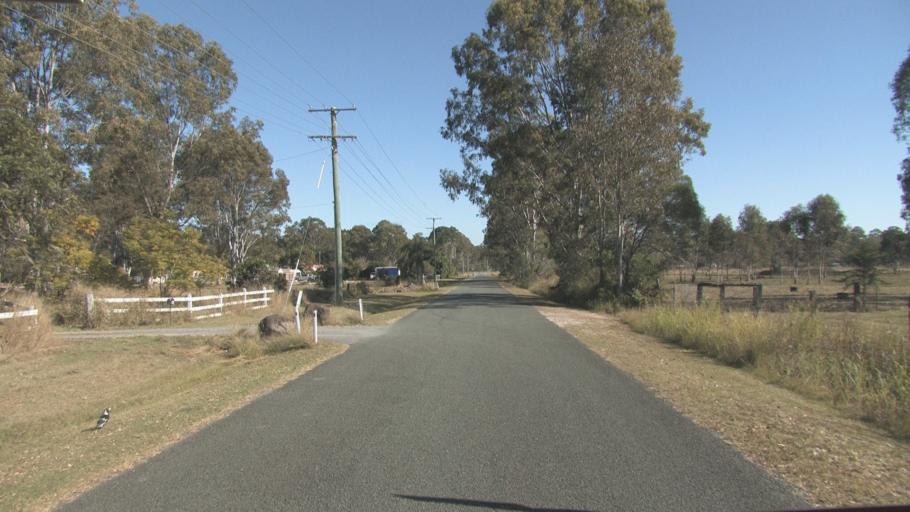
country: AU
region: Queensland
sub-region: Logan
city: Chambers Flat
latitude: -27.7839
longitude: 153.1389
